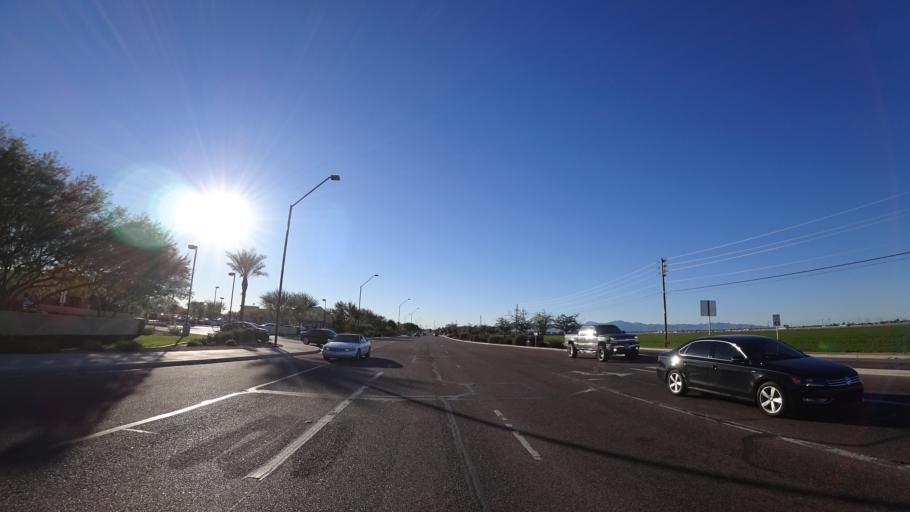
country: US
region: Arizona
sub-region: Maricopa County
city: Avondale
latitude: 33.4496
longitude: -112.3073
